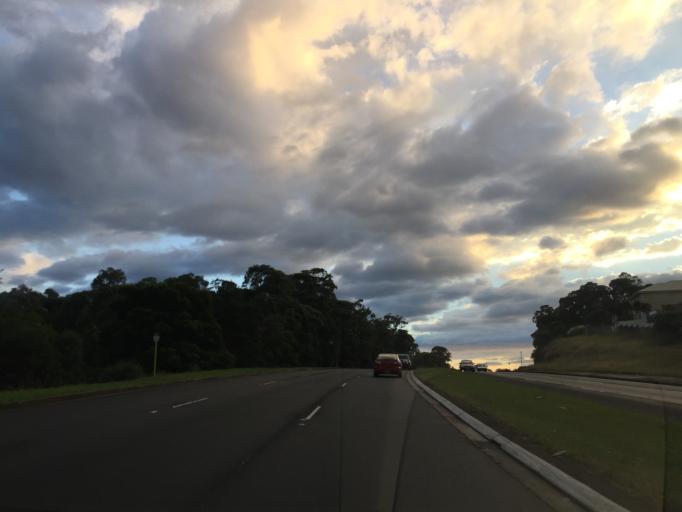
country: AU
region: New South Wales
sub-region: Shellharbour
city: Albion Park Rail
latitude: -34.5686
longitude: 150.8239
